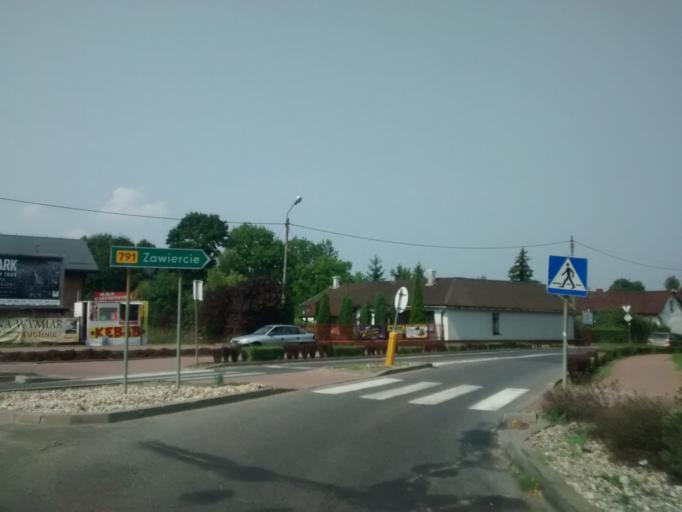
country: PL
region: Lesser Poland Voivodeship
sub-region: Powiat olkuski
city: Klucze
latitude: 50.3359
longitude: 19.5625
